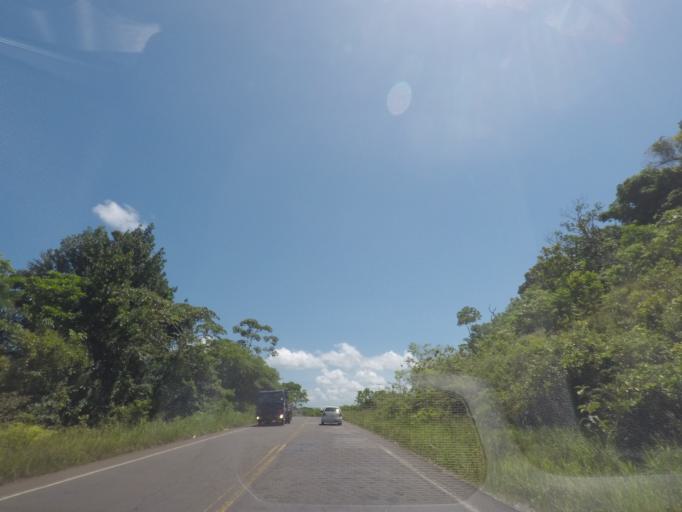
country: BR
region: Bahia
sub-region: Valenca
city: Valenca
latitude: -13.3313
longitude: -39.0549
